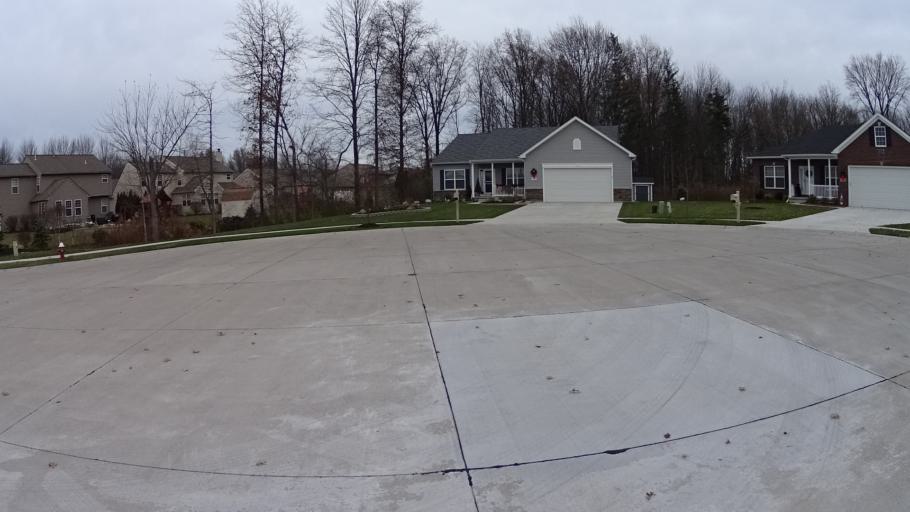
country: US
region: Ohio
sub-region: Lorain County
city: Avon
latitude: 41.4164
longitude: -82.0446
